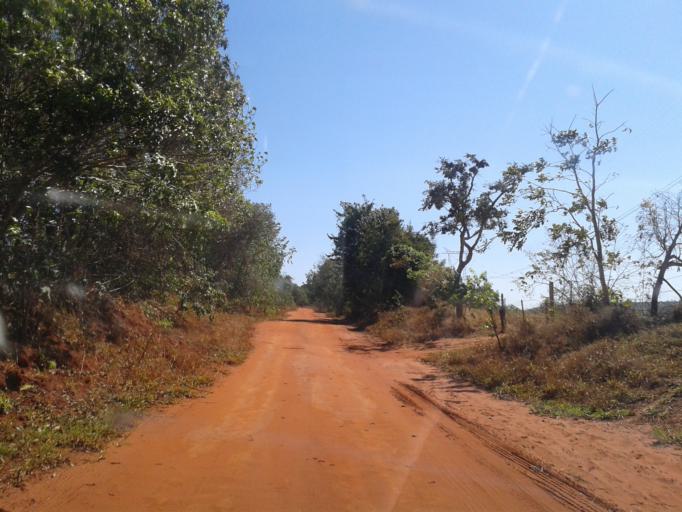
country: BR
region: Minas Gerais
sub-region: Monte Alegre De Minas
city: Monte Alegre de Minas
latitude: -18.8720
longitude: -49.1317
